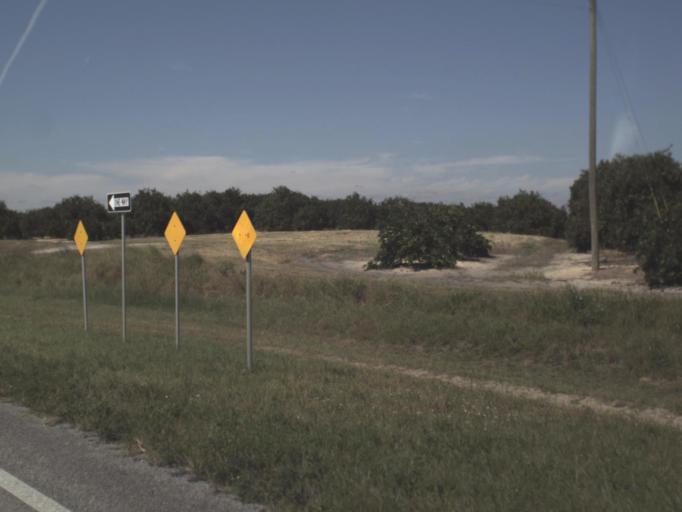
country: US
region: Florida
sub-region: Highlands County
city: Lake Placid
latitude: 27.3255
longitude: -81.3743
